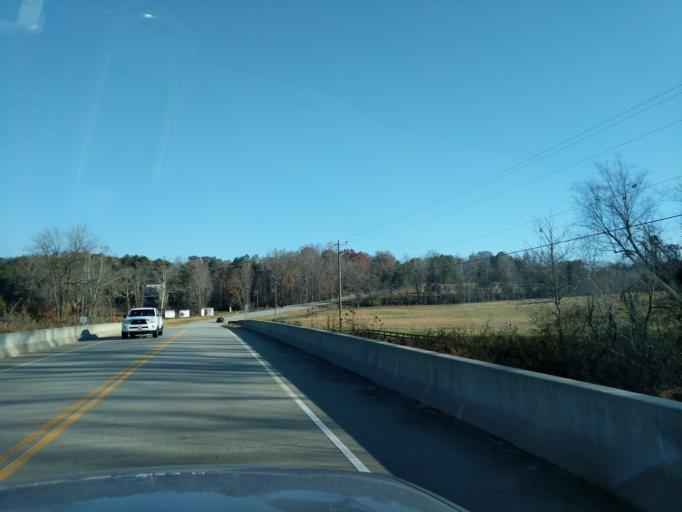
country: US
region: South Carolina
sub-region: Spartanburg County
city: Landrum
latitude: 35.1880
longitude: -82.1440
